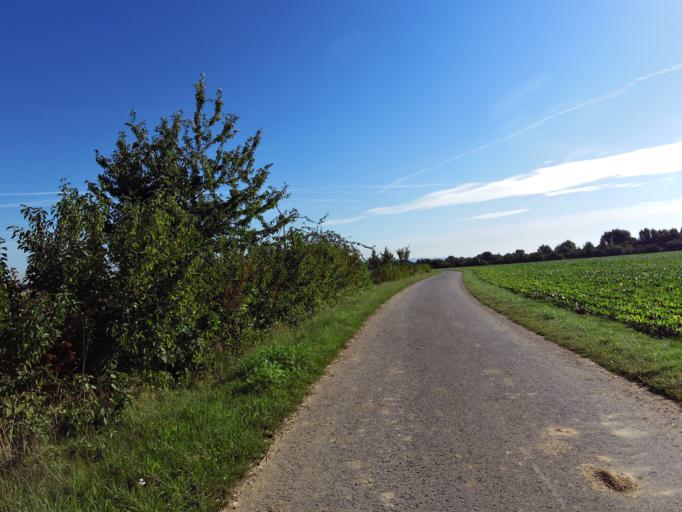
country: DE
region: North Rhine-Westphalia
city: Niedermerz
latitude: 50.8586
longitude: 6.2428
